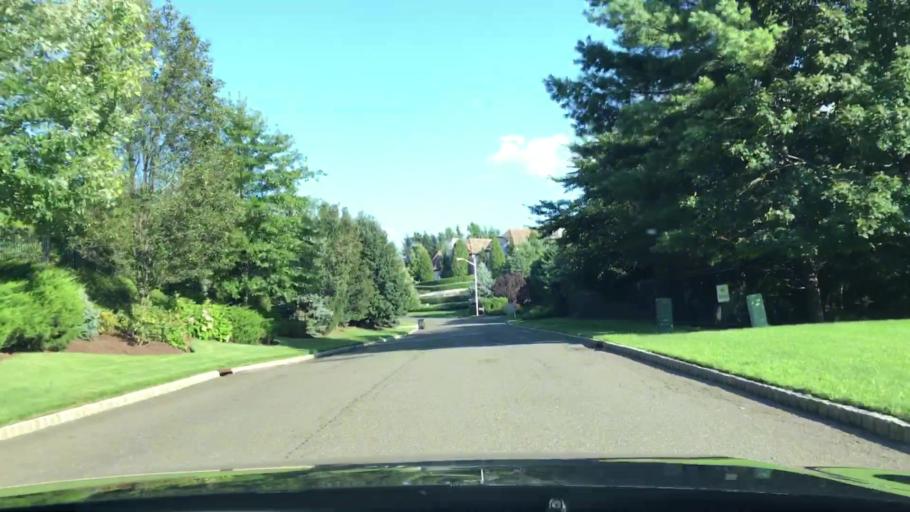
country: US
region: New Jersey
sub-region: Bergen County
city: Tenafly
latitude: 40.9279
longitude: -73.9438
